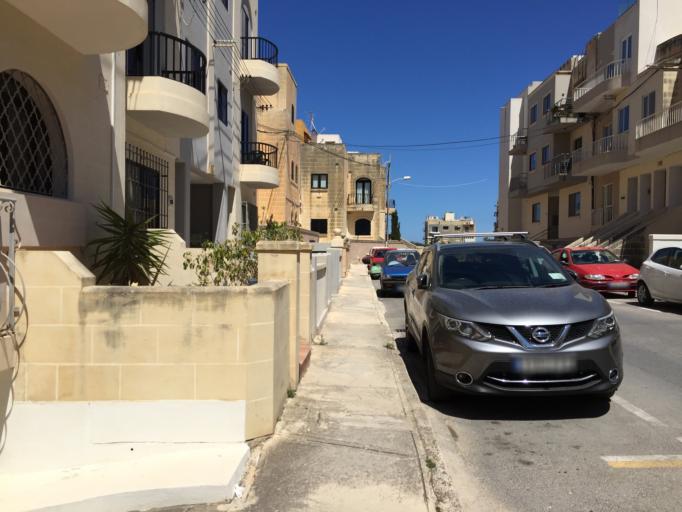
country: MT
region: Saint Julian
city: San Giljan
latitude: 35.9140
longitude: 14.4857
